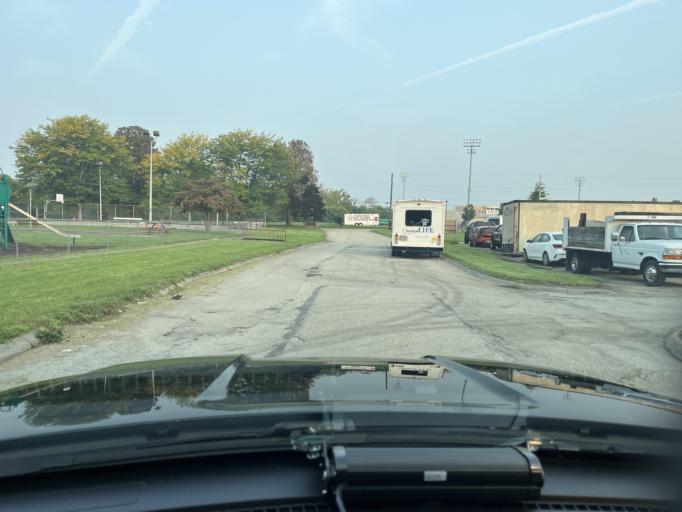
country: US
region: Pennsylvania
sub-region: Fayette County
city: Uniontown
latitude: 39.8930
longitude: -79.7189
